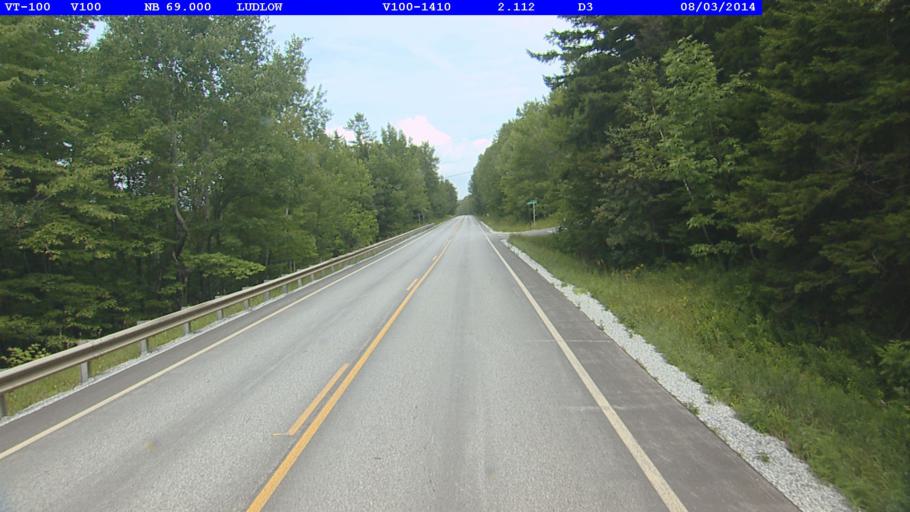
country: US
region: Vermont
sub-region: Windsor County
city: Chester
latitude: 43.3582
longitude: -72.7232
